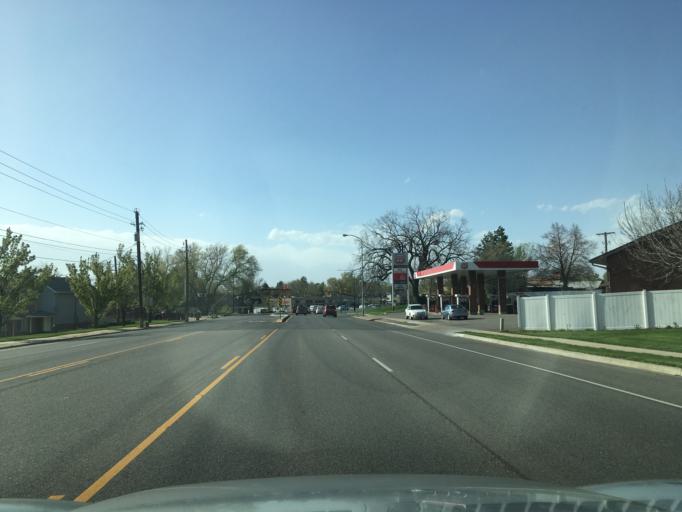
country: US
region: Utah
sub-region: Davis County
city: Kaysville
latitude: 41.0323
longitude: -111.9373
